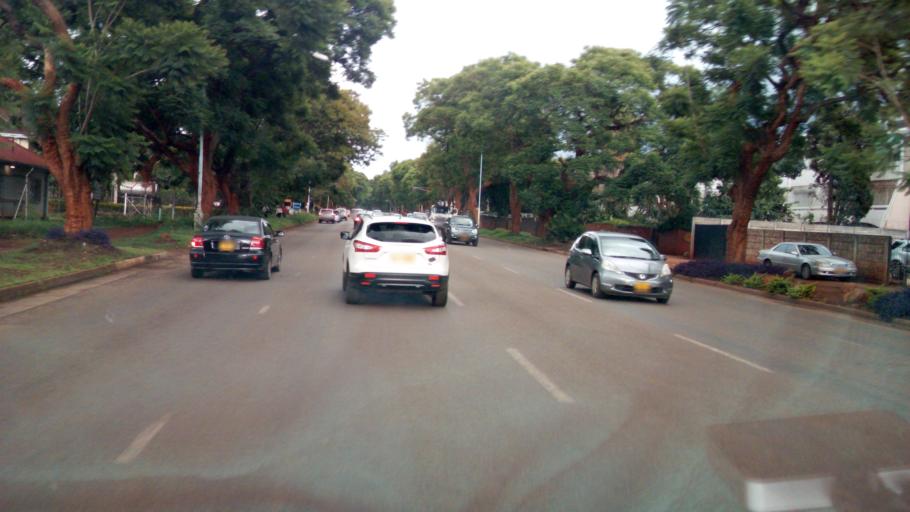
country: ZW
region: Harare
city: Harare
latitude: -17.8167
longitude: 31.0445
